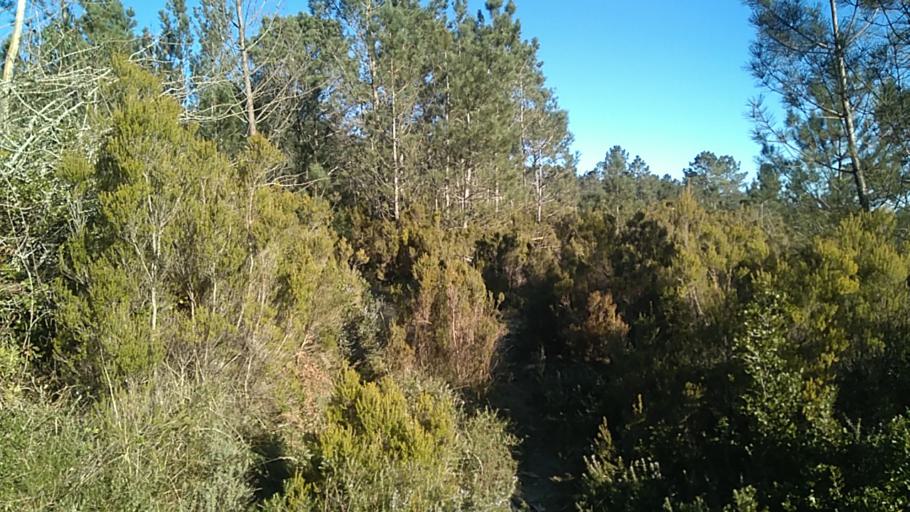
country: PT
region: Leiria
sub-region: Alcobaca
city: Aljubarrota
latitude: 39.5338
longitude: -8.8586
